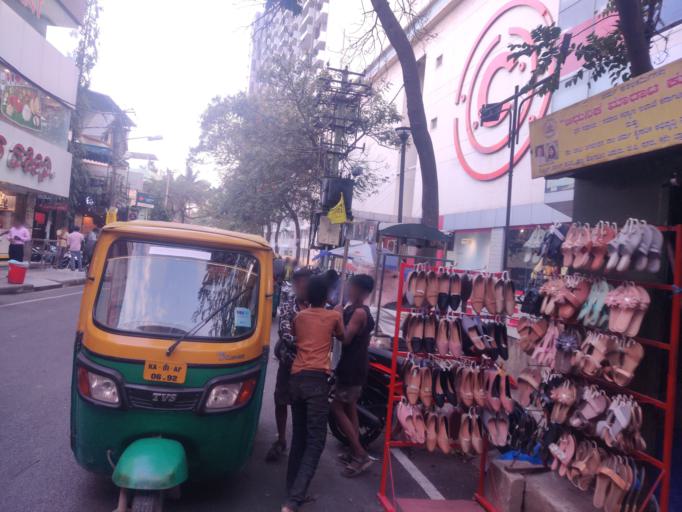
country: IN
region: Karnataka
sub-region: Bangalore Urban
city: Bangalore
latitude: 12.9167
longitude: 77.5927
